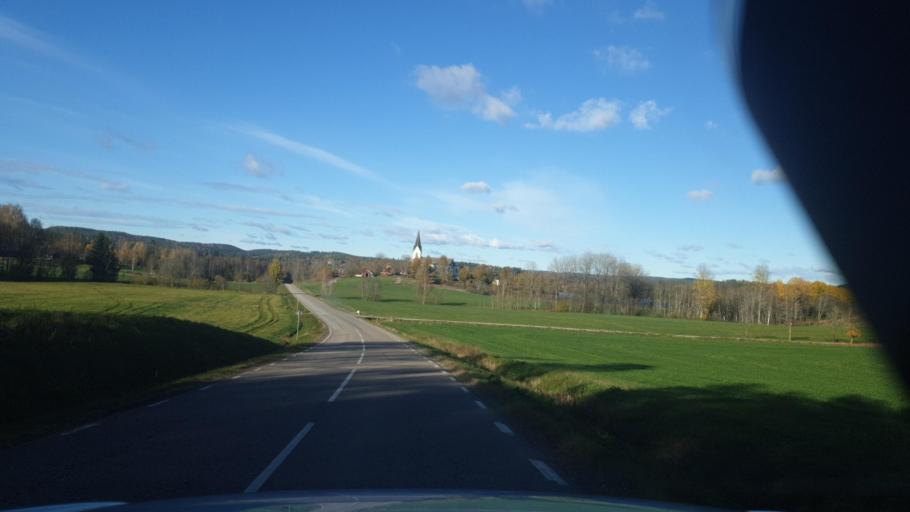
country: SE
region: Vaermland
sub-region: Arvika Kommun
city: Arvika
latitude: 59.6474
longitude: 12.8931
